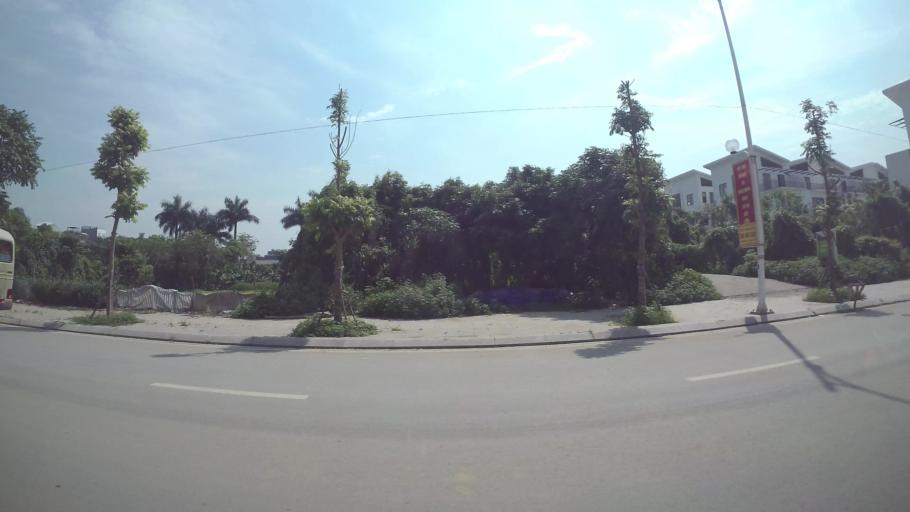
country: VN
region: Ha Noi
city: Hoan Kiem
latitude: 21.0609
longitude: 105.8688
